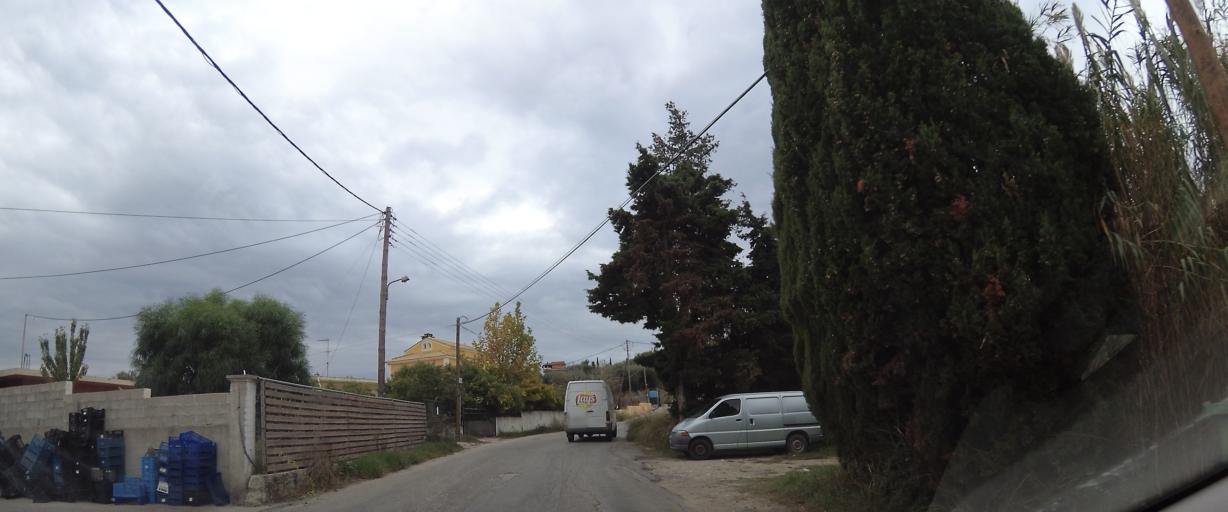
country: GR
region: Ionian Islands
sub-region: Nomos Kerkyras
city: Agios Georgis
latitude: 39.7372
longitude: 19.6735
